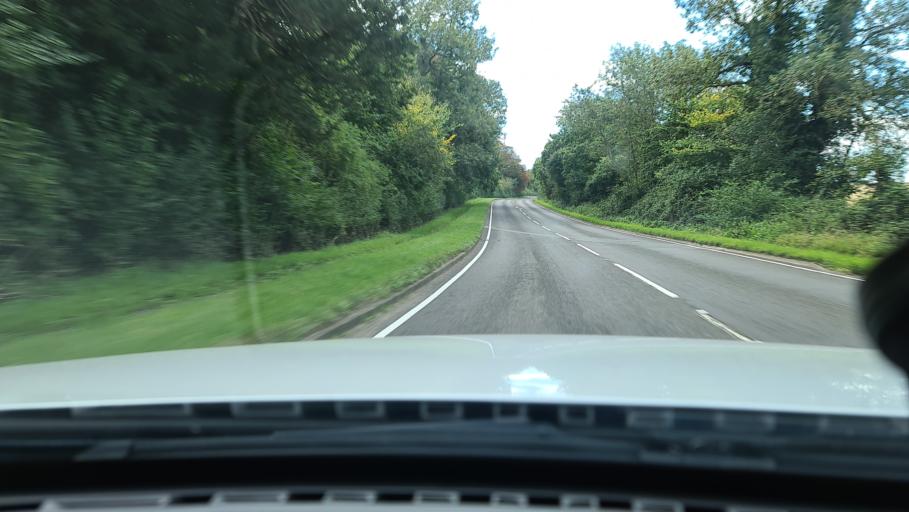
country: GB
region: England
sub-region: Warwickshire
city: Shipston on Stour
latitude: 52.0816
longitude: -1.6240
